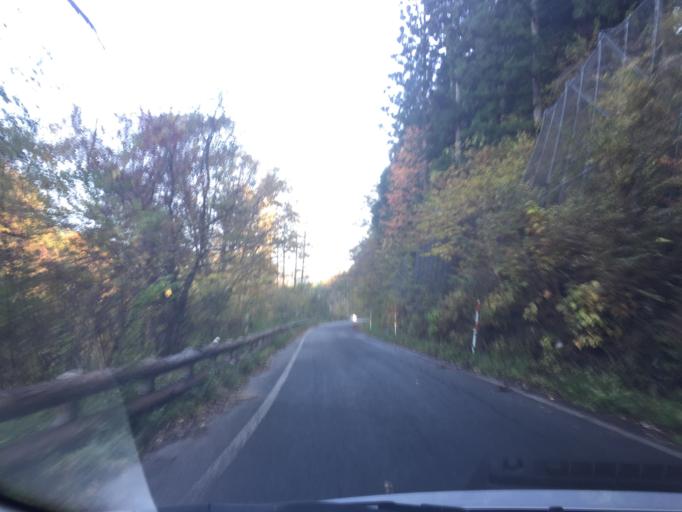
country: JP
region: Nagano
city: Iida
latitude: 35.3720
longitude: 137.6945
